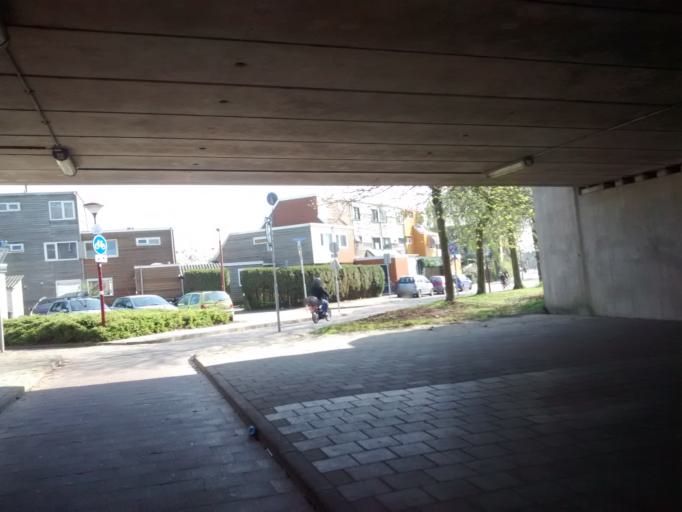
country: NL
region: Utrecht
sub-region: Gemeente Nieuwegein
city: Nieuwegein
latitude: 52.0261
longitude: 5.0945
